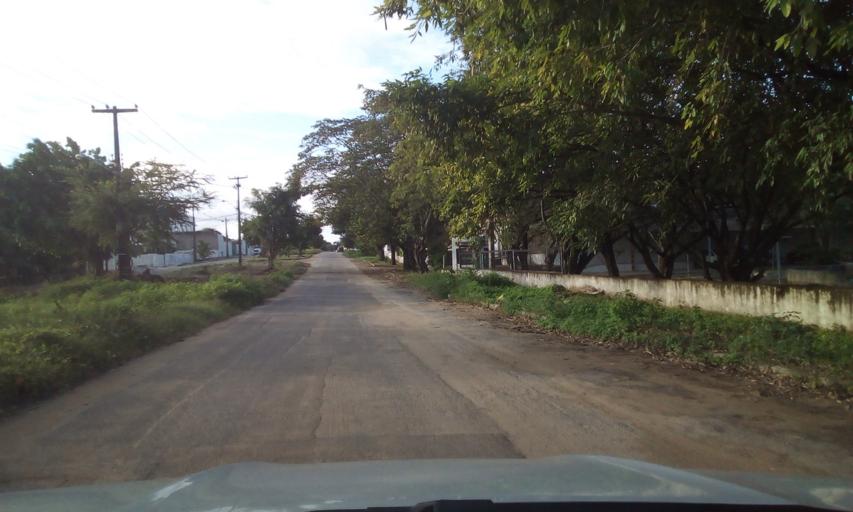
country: BR
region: Paraiba
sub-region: Joao Pessoa
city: Joao Pessoa
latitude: -7.1659
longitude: -34.8229
